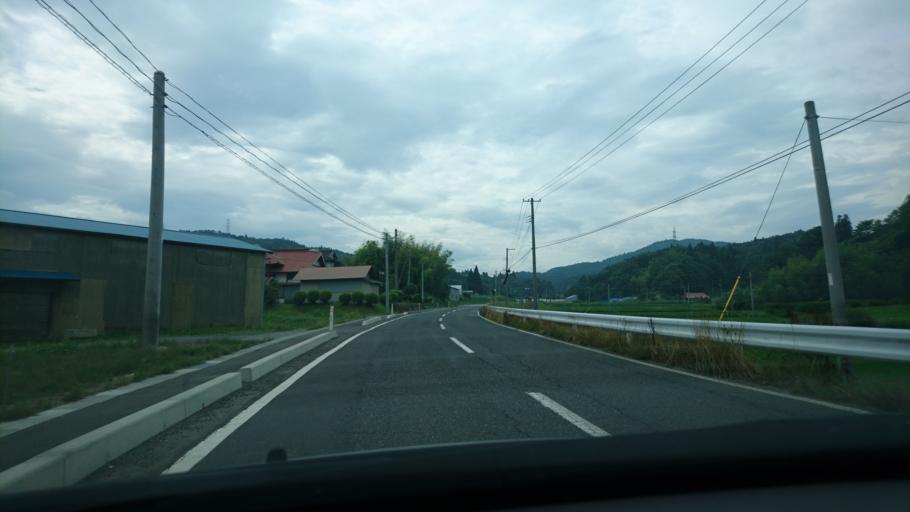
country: JP
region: Iwate
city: Ichinoseki
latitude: 38.8990
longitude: 141.4251
